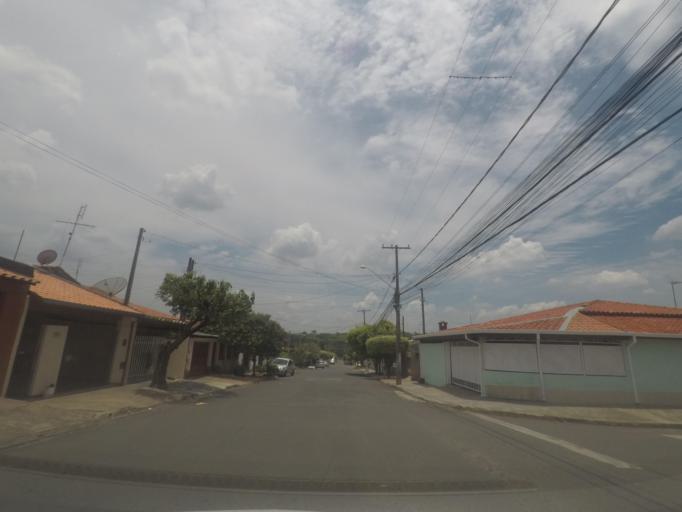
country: BR
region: Sao Paulo
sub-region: Nova Odessa
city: Nova Odessa
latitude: -22.7943
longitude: -47.2776
